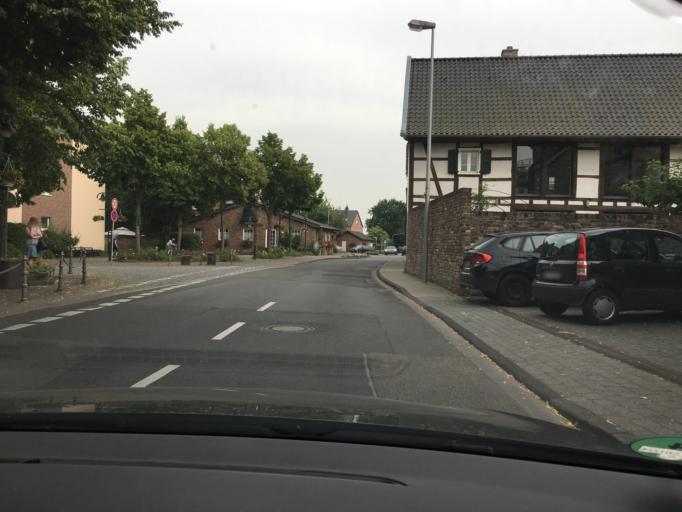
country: DE
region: North Rhine-Westphalia
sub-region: Regierungsbezirk Koln
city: Pulheim
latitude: 50.9576
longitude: 6.7648
